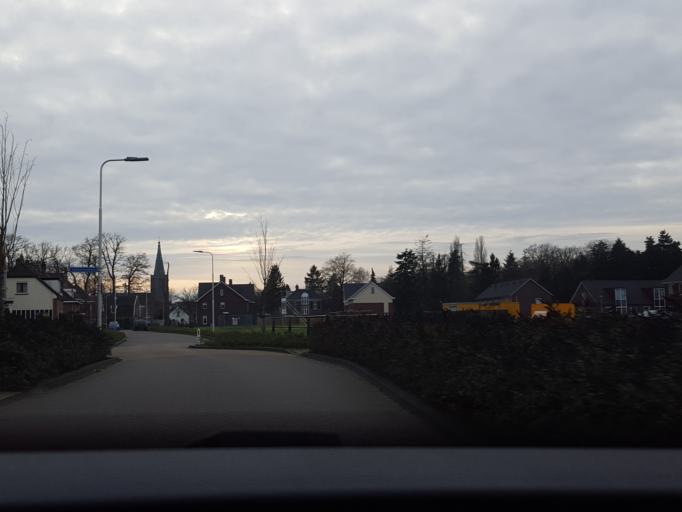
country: NL
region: Gelderland
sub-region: Berkelland
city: Eibergen
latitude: 52.0464
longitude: 6.6211
